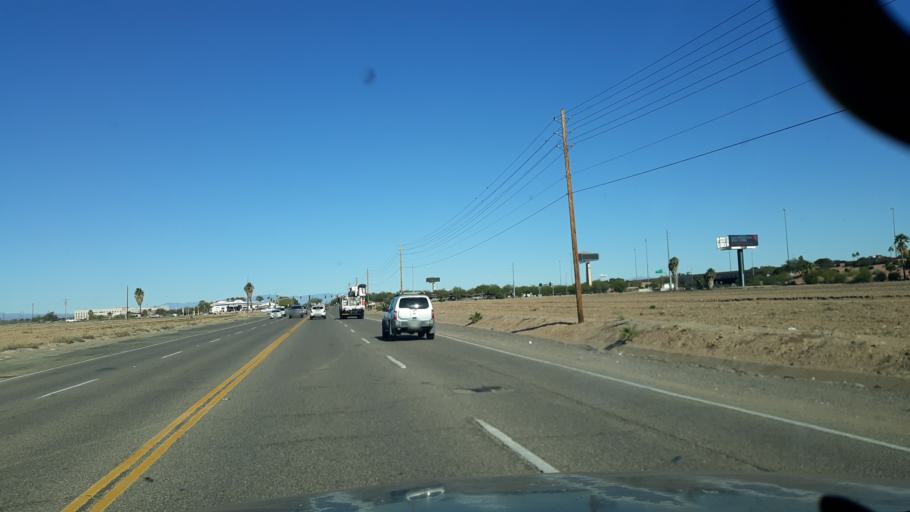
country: US
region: Arizona
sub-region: Maricopa County
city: Peoria
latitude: 33.5335
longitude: -112.2724
